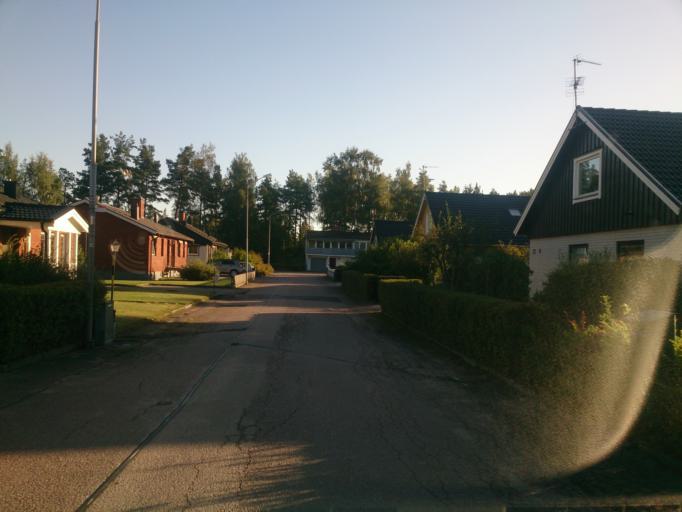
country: SE
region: OEstergoetland
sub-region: Atvidabergs Kommun
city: Atvidaberg
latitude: 58.2053
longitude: 15.9793
